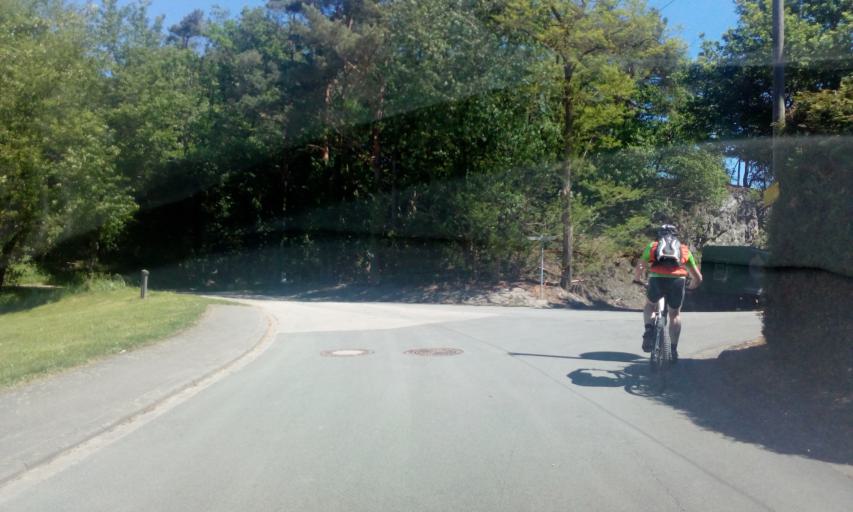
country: DE
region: Rheinland-Pfalz
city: Trittenheim
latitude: 49.8130
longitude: 6.9061
